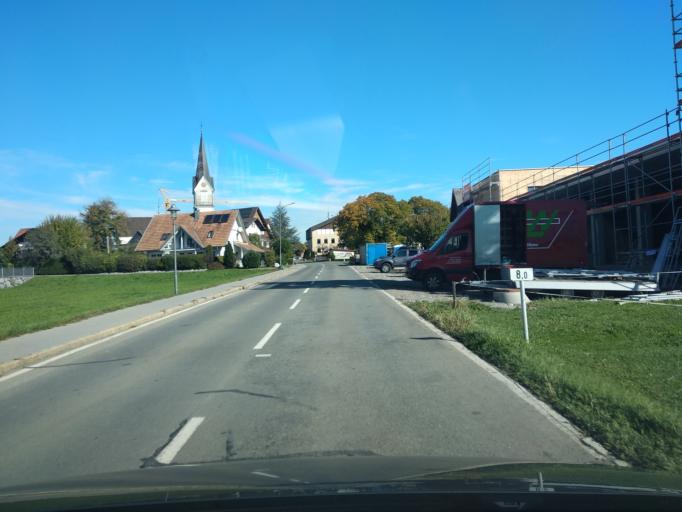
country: AT
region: Vorarlberg
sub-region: Politischer Bezirk Bregenz
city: Hohenweiler
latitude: 47.5866
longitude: 9.7803
